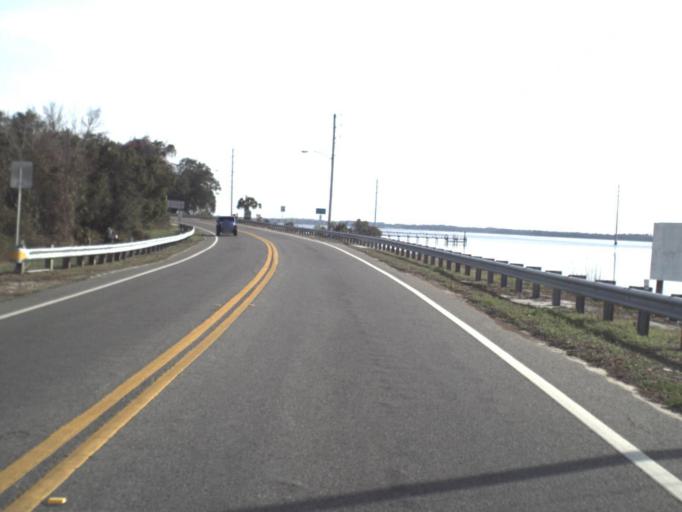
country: US
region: Florida
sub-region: Bay County
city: Parker
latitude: 30.1360
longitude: -85.6156
